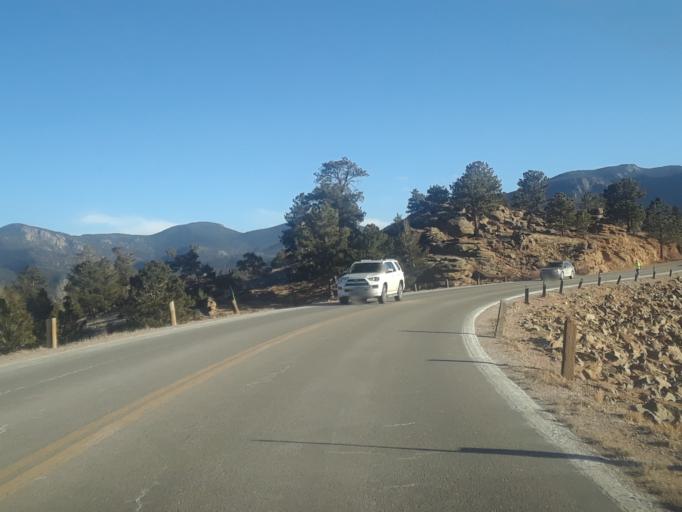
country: US
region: Colorado
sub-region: Larimer County
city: Estes Park
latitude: 40.3462
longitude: -105.5307
